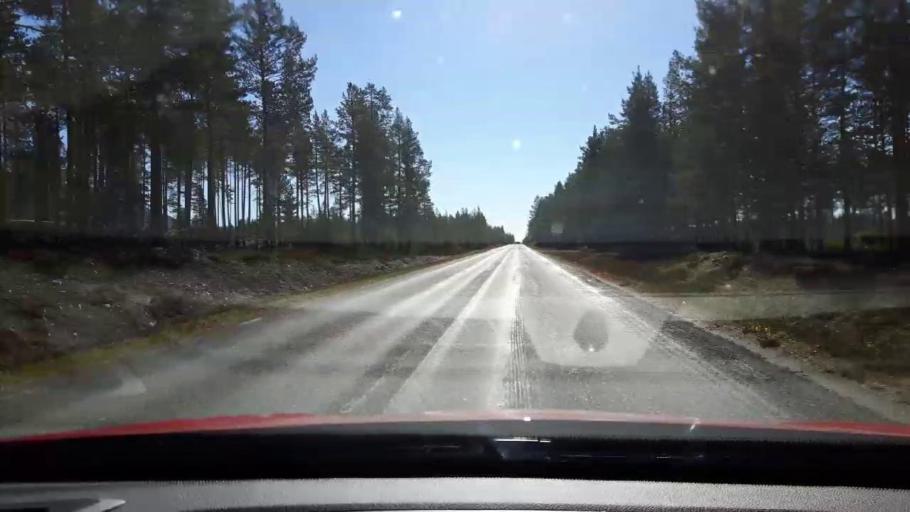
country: SE
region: Jaemtland
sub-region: Harjedalens Kommun
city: Sveg
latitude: 62.4150
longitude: 13.9150
